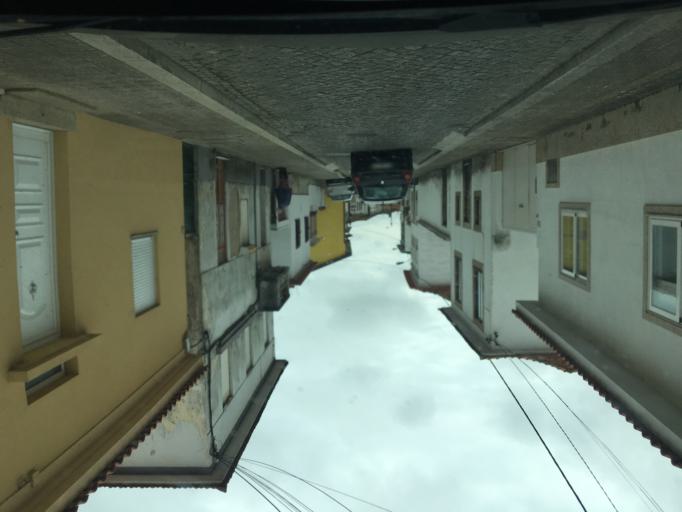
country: PT
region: Porto
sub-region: Matosinhos
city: Santa Cruz do Bispo
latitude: 41.2238
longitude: -8.6767
